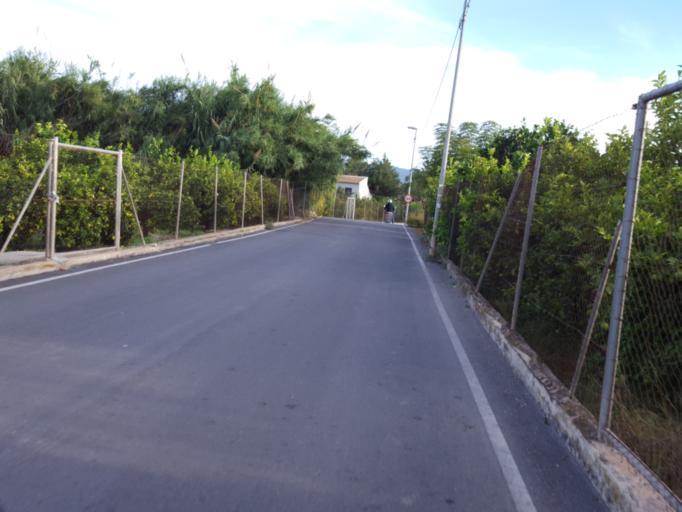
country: ES
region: Murcia
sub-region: Murcia
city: Murcia
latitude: 37.9937
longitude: -1.1746
